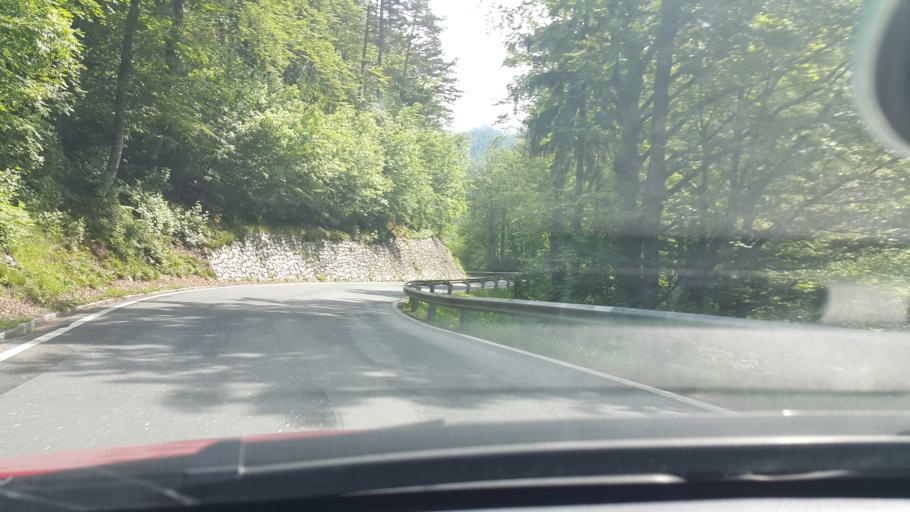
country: AT
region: Carinthia
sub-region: Politischer Bezirk Klagenfurt Land
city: Ferlach
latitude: 46.4888
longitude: 14.2717
